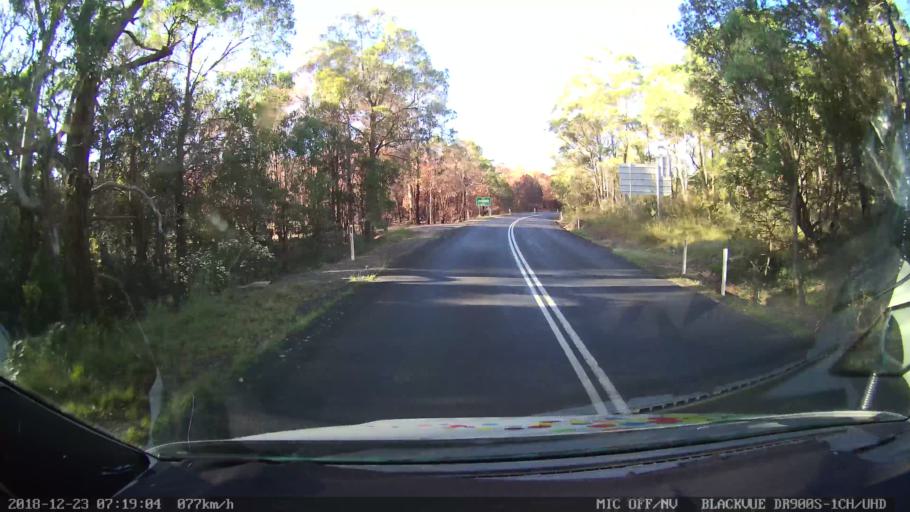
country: AU
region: New South Wales
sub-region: Bellingen
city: Dorrigo
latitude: -30.4823
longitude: 152.2910
